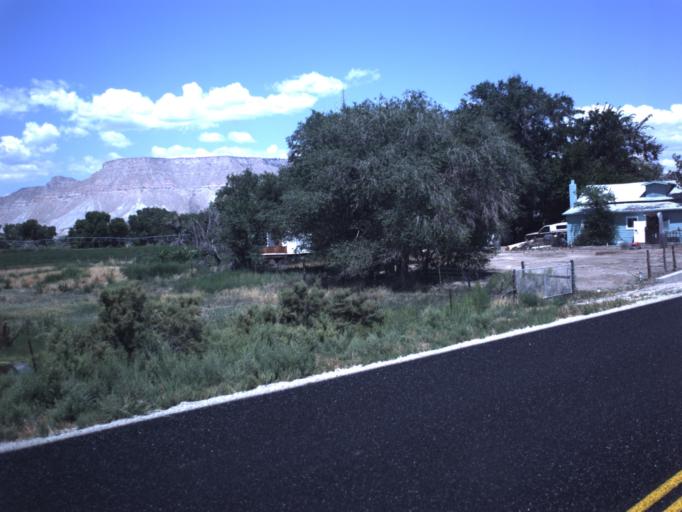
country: US
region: Utah
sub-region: Emery County
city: Ferron
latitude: 39.0715
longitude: -111.1315
